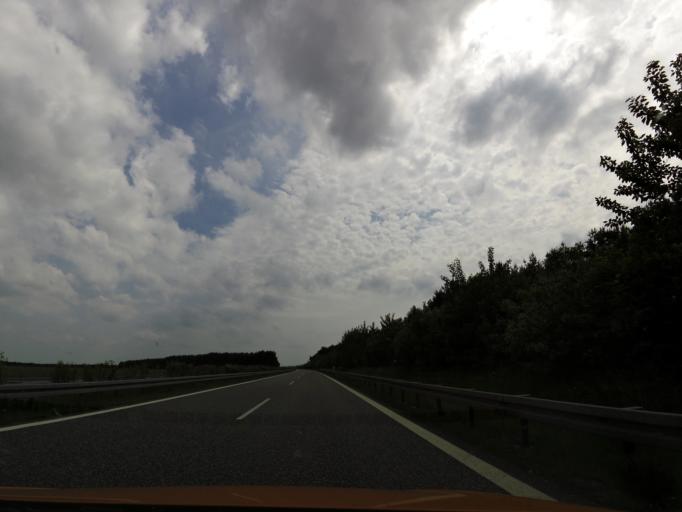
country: DE
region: Mecklenburg-Vorpommern
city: Mirow
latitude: 53.4935
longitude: 11.4784
